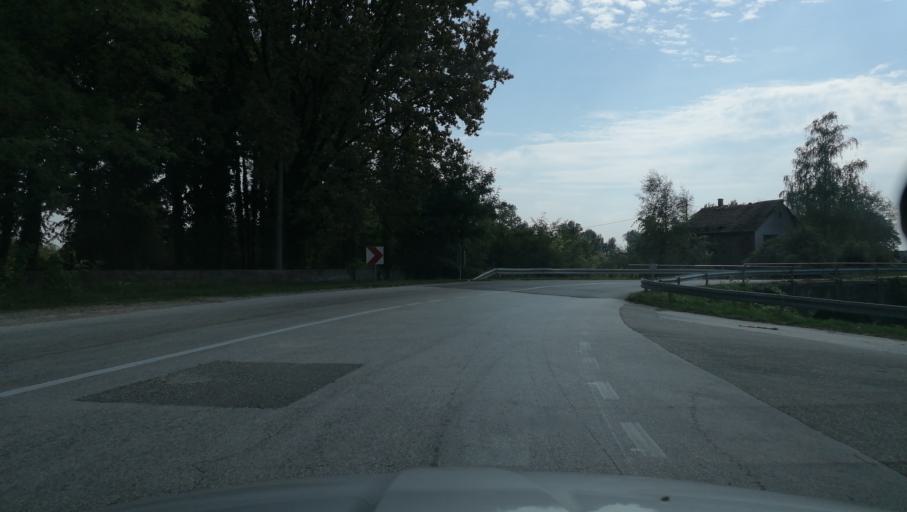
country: BA
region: Republika Srpska
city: Balatun
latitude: 44.8928
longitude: 19.3349
